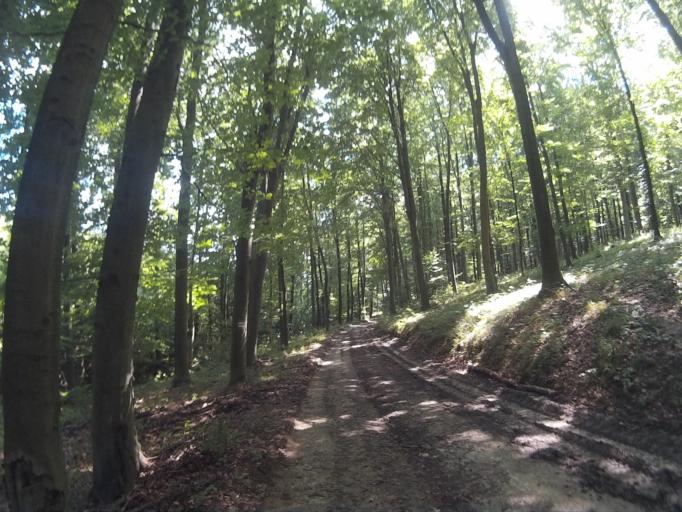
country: HU
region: Veszprem
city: Zirc
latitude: 47.2038
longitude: 17.9051
